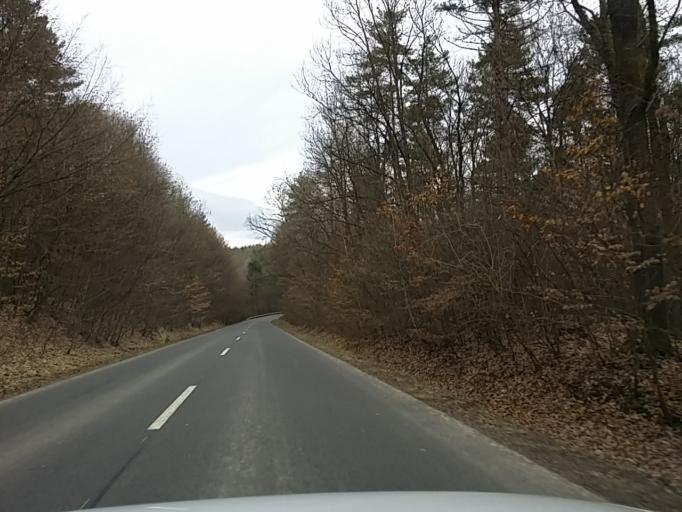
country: HU
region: Borsod-Abauj-Zemplen
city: Putnok
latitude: 48.4512
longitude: 20.4799
